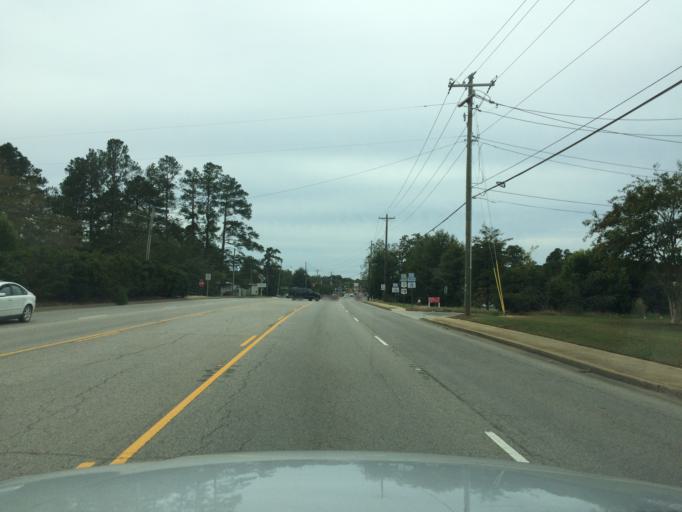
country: US
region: South Carolina
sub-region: Aiken County
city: Aiken
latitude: 33.5799
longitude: -81.7018
